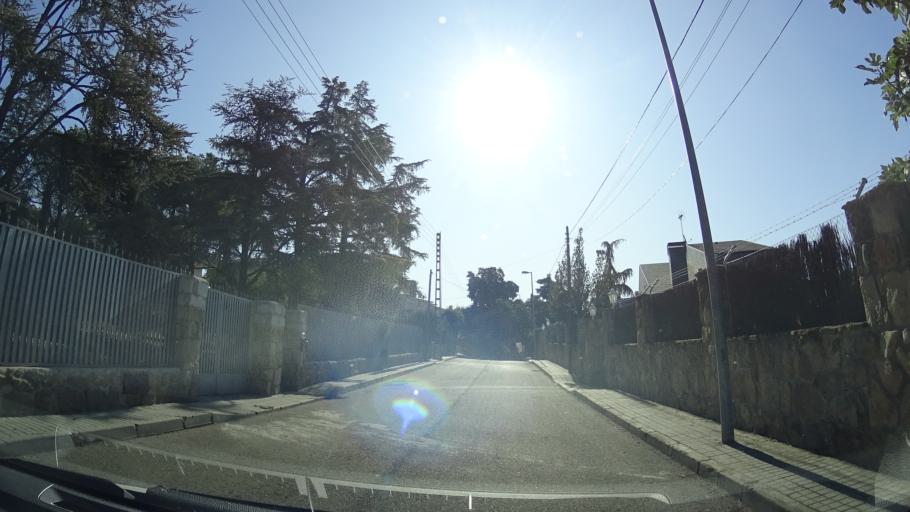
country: ES
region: Madrid
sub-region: Provincia de Madrid
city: Colmenarejo
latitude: 40.5582
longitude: -4.0198
